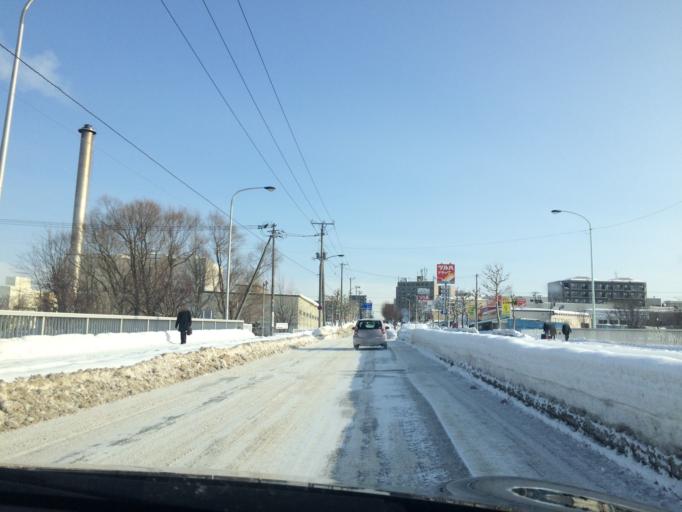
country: JP
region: Hokkaido
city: Ebetsu
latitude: 43.0416
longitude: 141.4778
